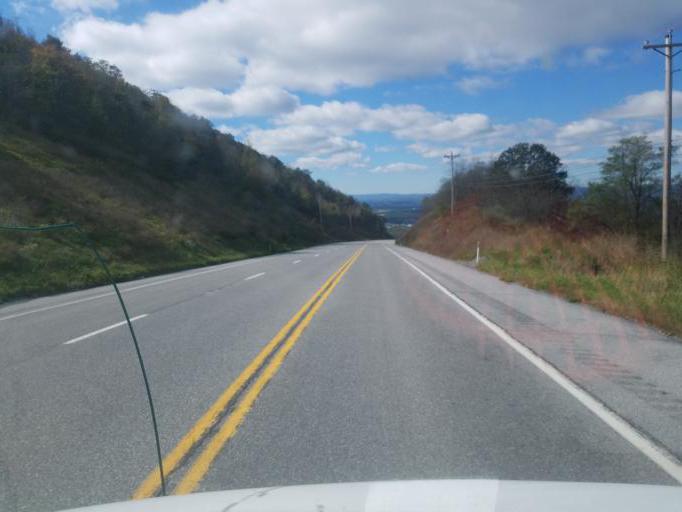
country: US
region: Pennsylvania
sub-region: Bedford County
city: Earlston
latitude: 40.0129
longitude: -78.2033
